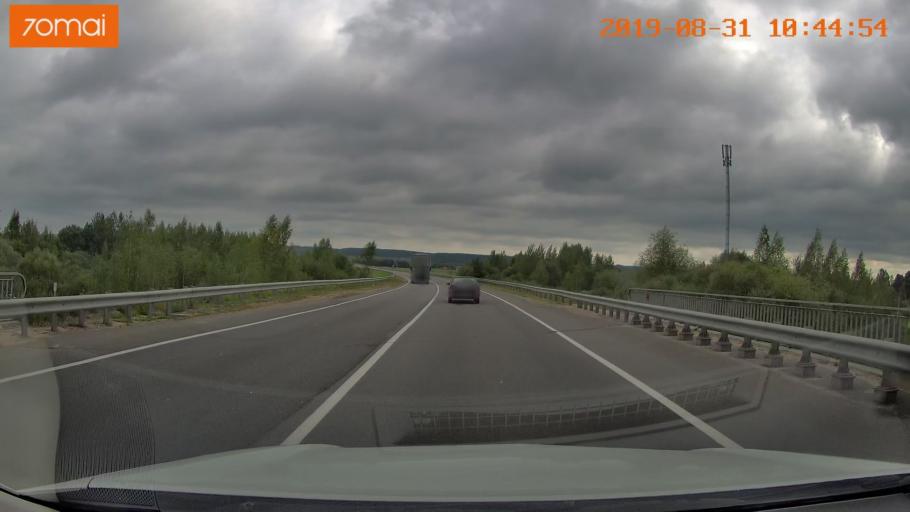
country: BY
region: Mogilev
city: Palykavichy Pyershyya
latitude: 53.9705
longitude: 30.3671
